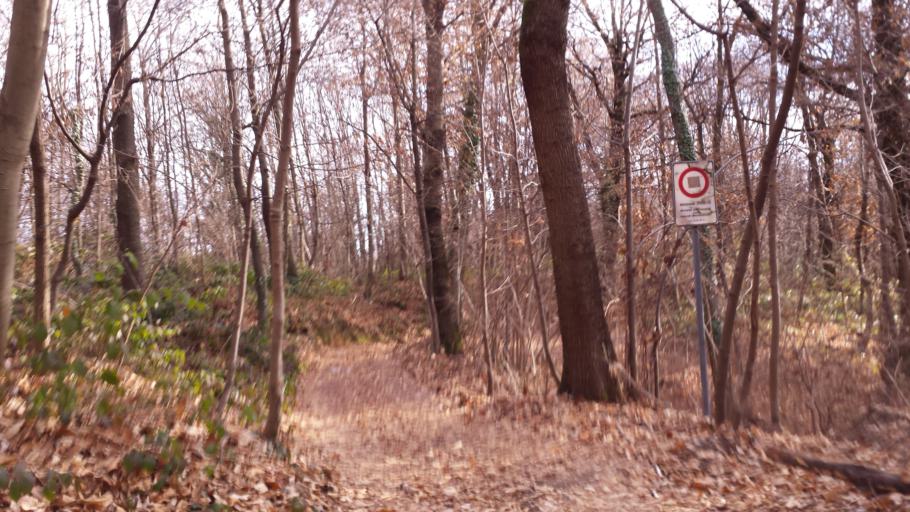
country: IT
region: Veneto
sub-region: Provincia di Treviso
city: Paderno del Grappa
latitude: 45.8497
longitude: 11.8534
